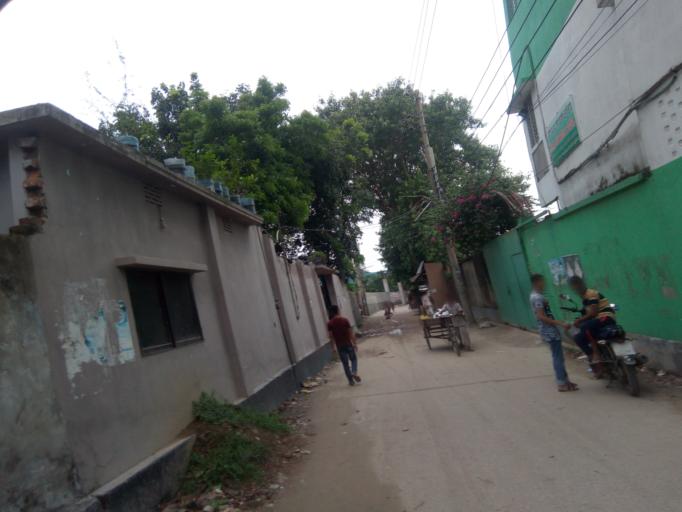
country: BD
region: Dhaka
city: Azimpur
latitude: 23.7353
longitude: 90.3559
